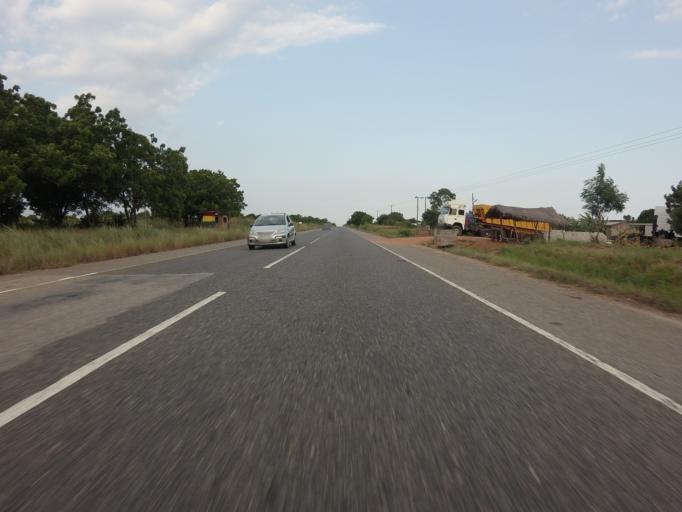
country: GH
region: Volta
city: Anloga
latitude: 6.0868
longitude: 0.5467
